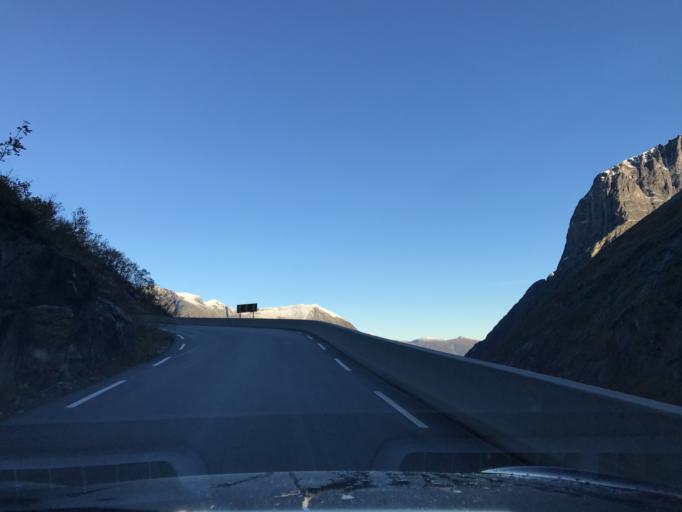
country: NO
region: More og Romsdal
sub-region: Rauma
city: Andalsnes
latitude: 62.4595
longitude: 7.6708
